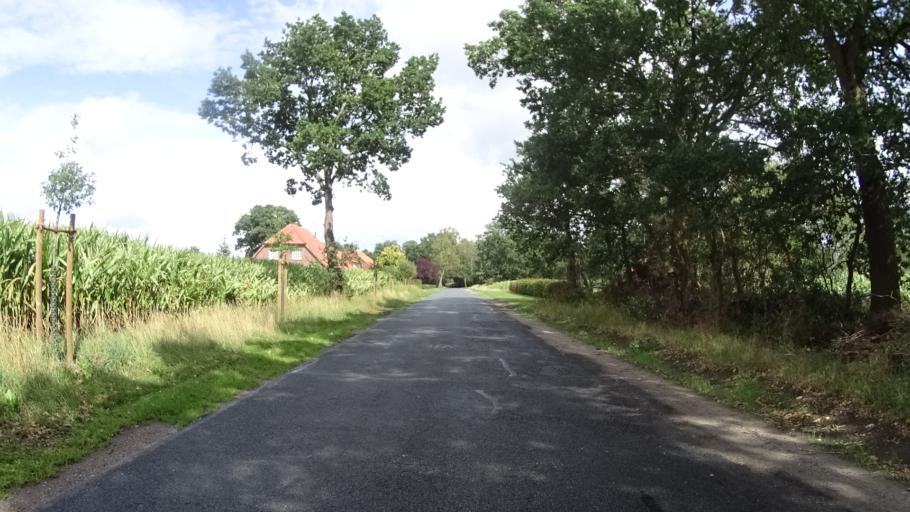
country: DE
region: Lower Saxony
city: Zetel
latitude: 53.3874
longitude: 7.9110
